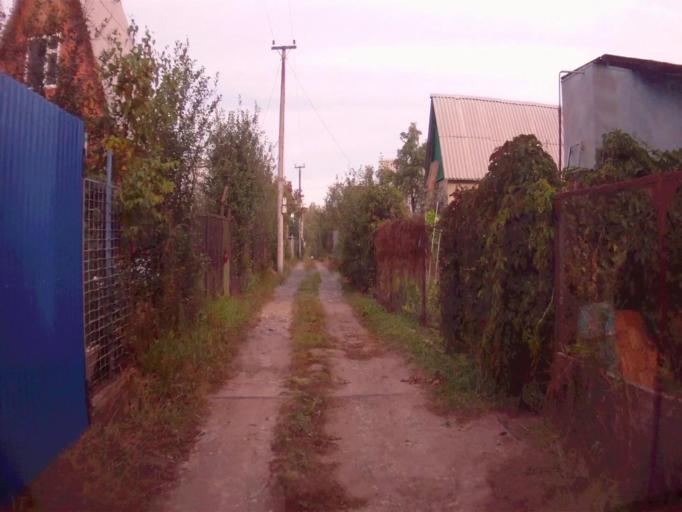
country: RU
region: Chelyabinsk
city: Sargazy
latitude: 55.1299
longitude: 61.2482
